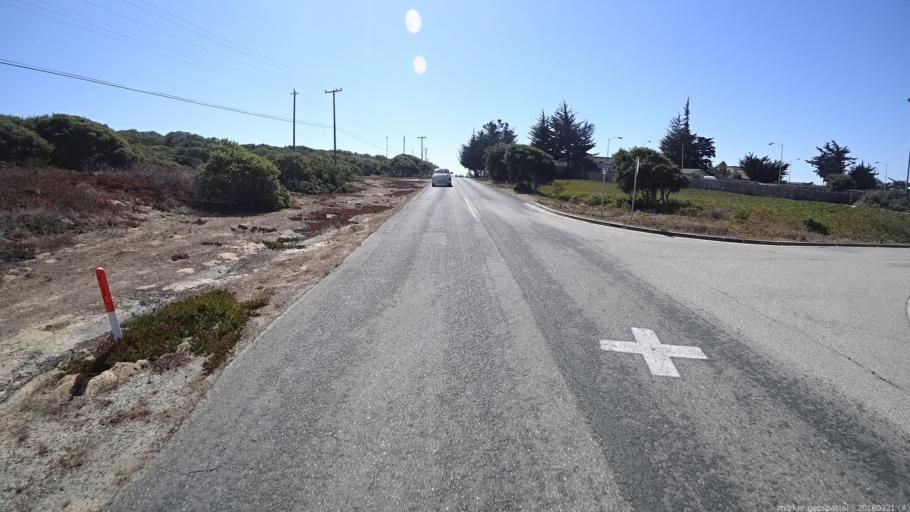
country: US
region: California
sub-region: Monterey County
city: Marina
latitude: 36.6499
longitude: -121.7869
